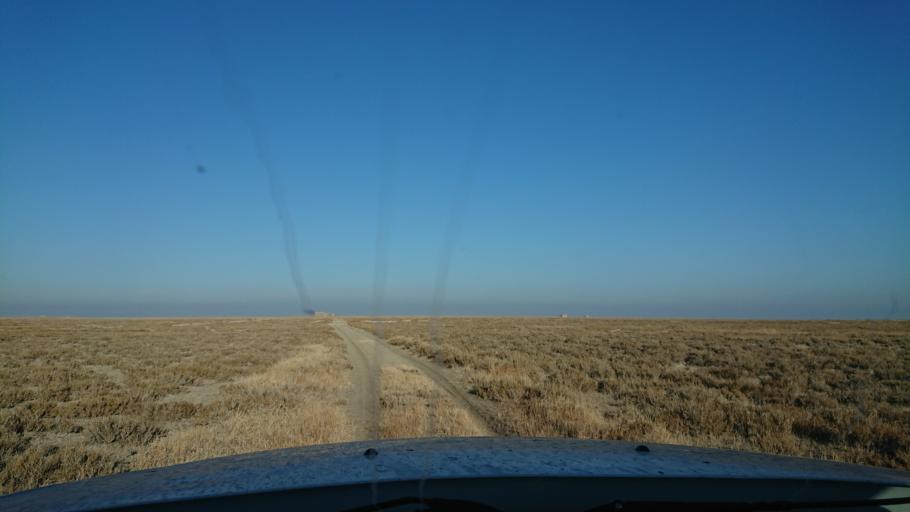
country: TR
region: Aksaray
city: Sultanhani
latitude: 38.3873
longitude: 33.5913
